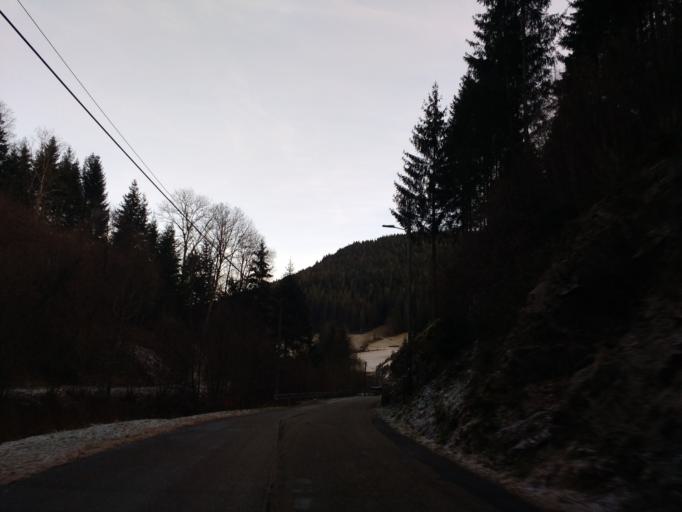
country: DE
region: Baden-Wuerttemberg
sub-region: Karlsruhe Region
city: Bad Rippoldsau-Schapbach
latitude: 48.4488
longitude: 8.2914
